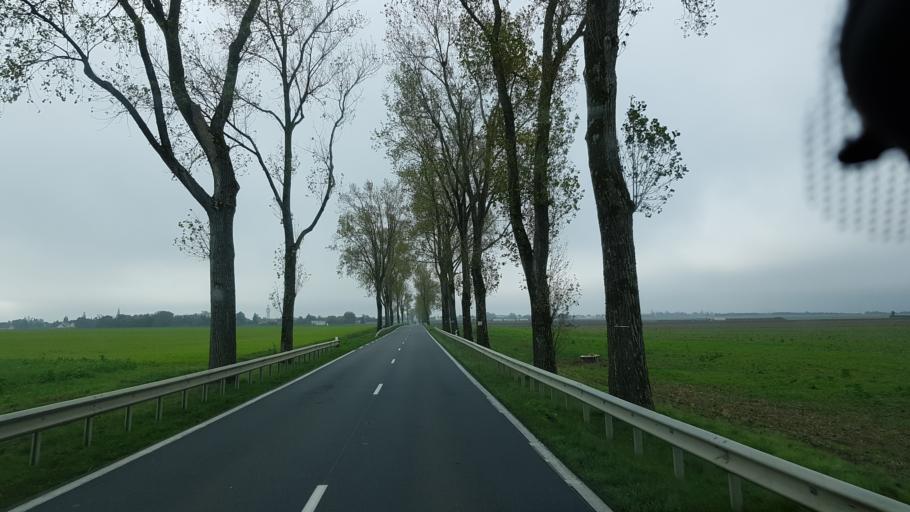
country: FR
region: Ile-de-France
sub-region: Departement de l'Essonne
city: Corbreuse
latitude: 48.4387
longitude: 1.9588
